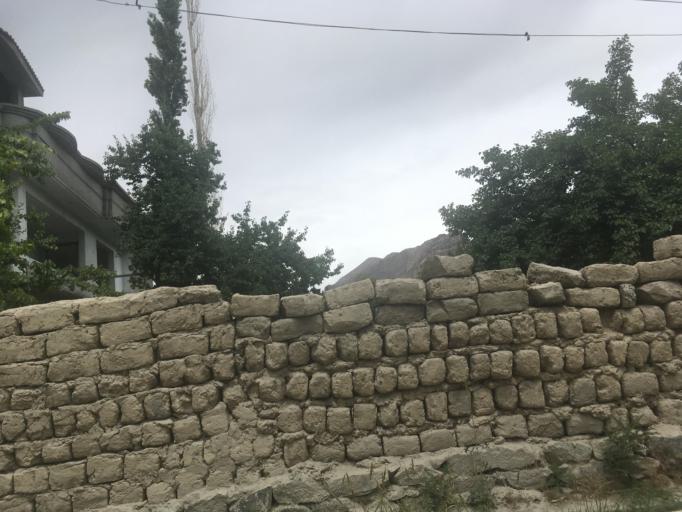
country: PK
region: Gilgit-Baltistan
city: Skardu
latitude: 35.2910
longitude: 75.6462
